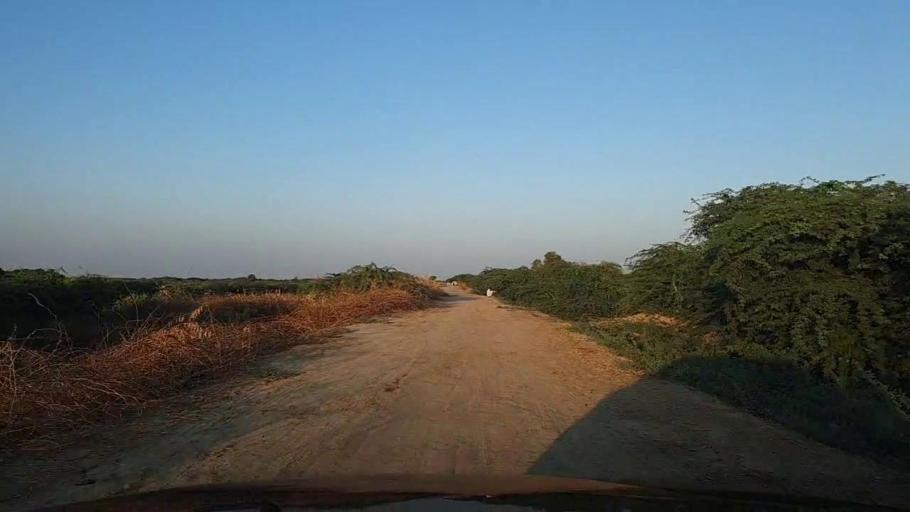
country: PK
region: Sindh
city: Thatta
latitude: 24.7205
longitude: 67.9427
